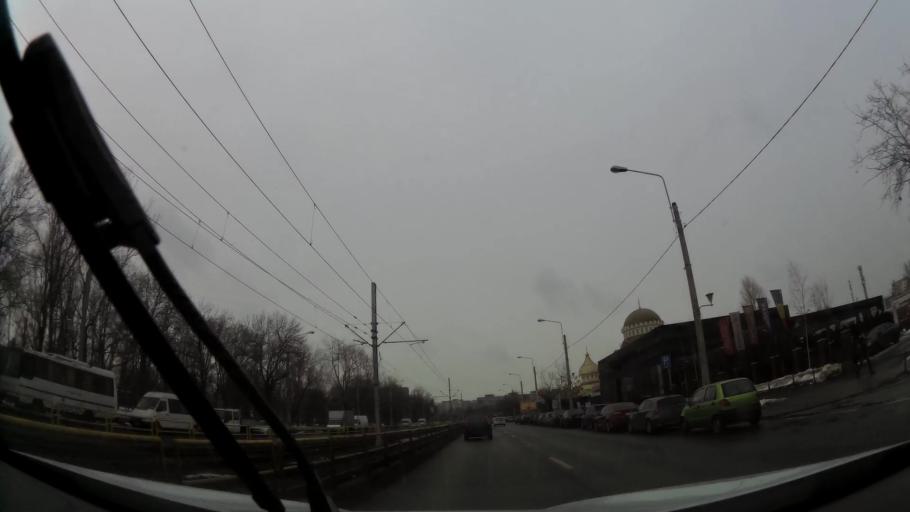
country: RO
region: Ilfov
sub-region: Comuna Chiajna
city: Rosu
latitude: 44.4194
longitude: 26.0346
